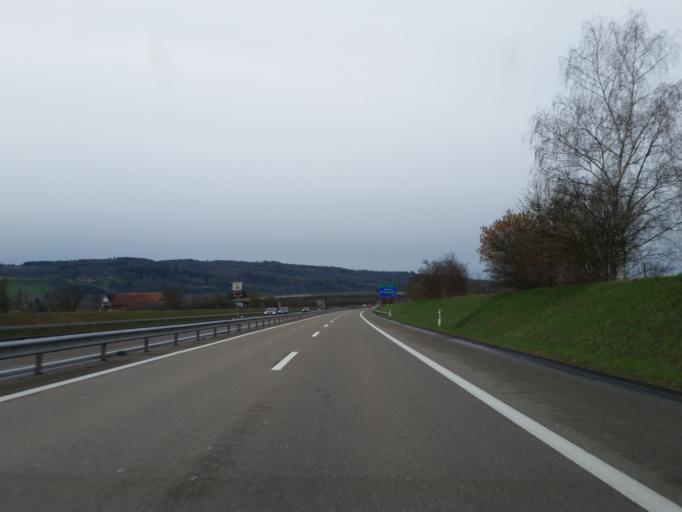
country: CH
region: Thurgau
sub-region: Frauenfeld District
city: Mullheim
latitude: 47.5968
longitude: 9.0097
